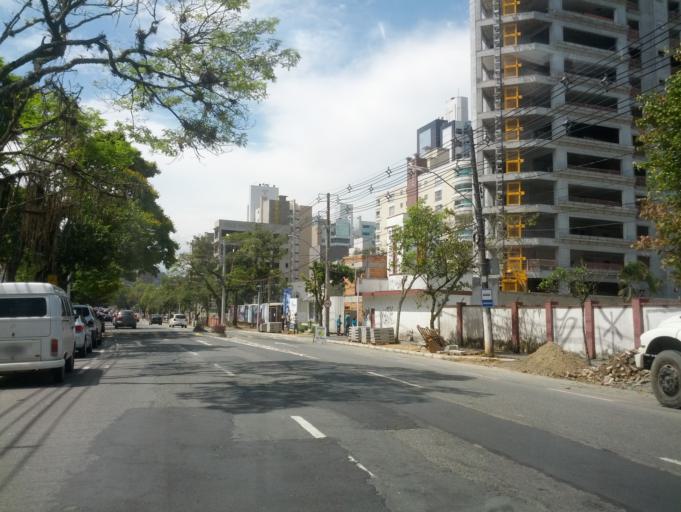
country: BR
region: Santa Catarina
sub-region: Blumenau
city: Blumenau
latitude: -26.9280
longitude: -49.0621
